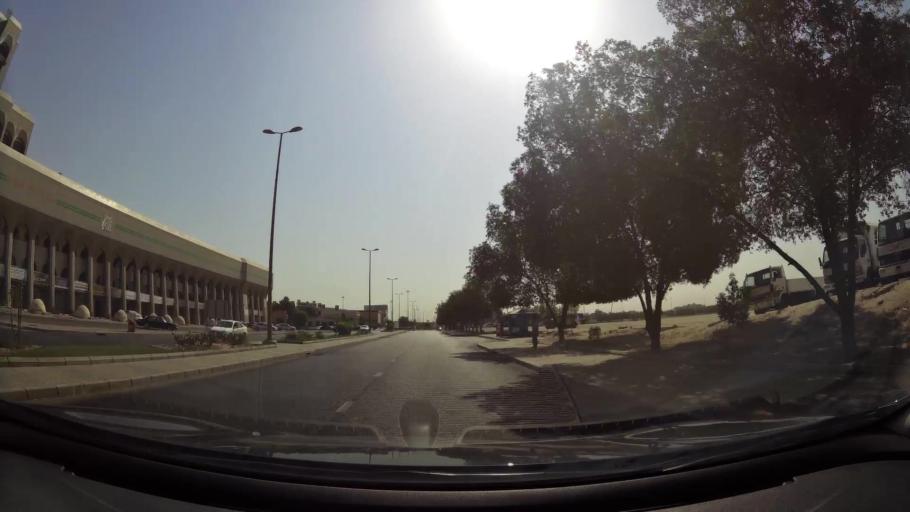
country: KW
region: Al Asimah
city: Kuwait City
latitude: 29.3685
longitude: 47.9869
